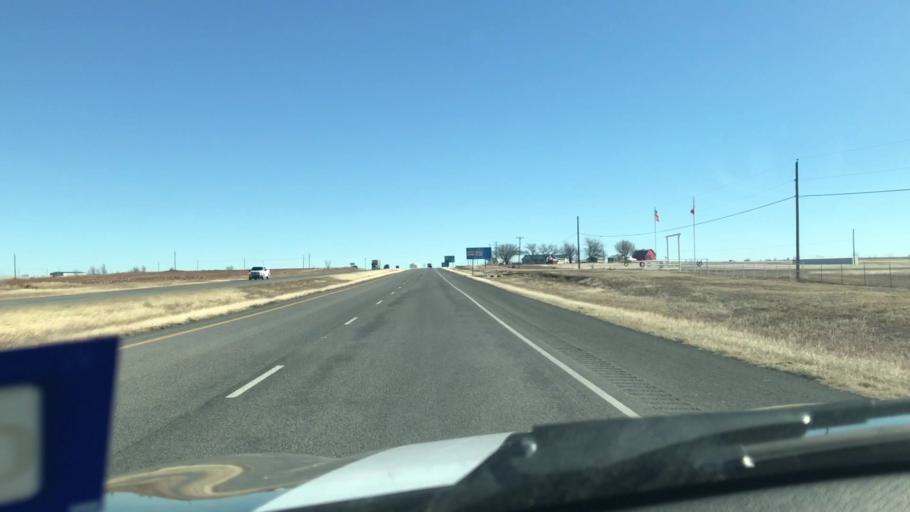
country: US
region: Texas
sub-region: Scurry County
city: Snyder
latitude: 32.7149
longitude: -100.8778
